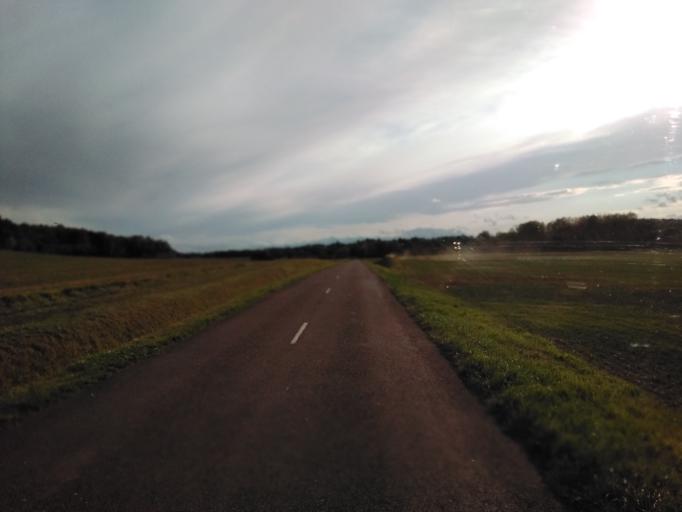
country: FR
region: Champagne-Ardenne
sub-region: Departement de l'Aube
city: Les Riceys
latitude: 47.8871
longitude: 4.3602
